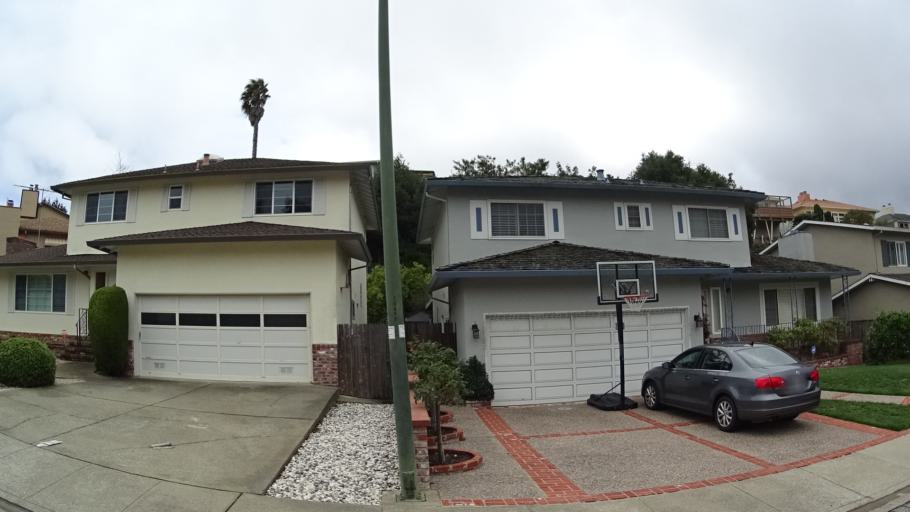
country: US
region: California
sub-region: San Mateo County
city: Millbrae
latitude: 37.5975
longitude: -122.4076
